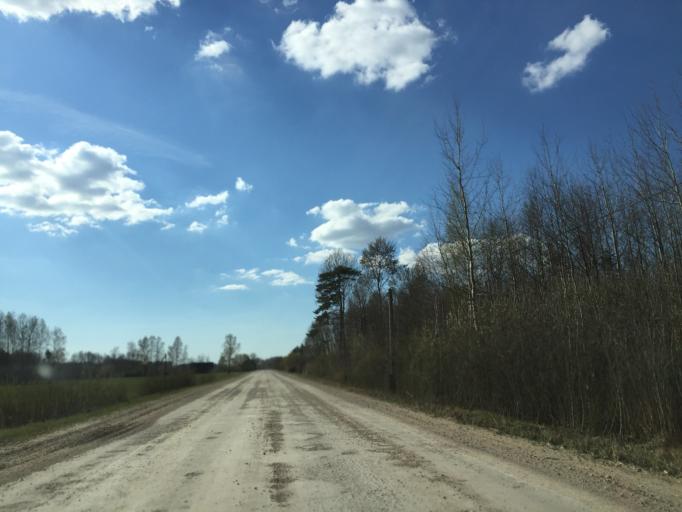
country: LV
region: Krimulda
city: Ragana
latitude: 57.3426
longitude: 24.6084
